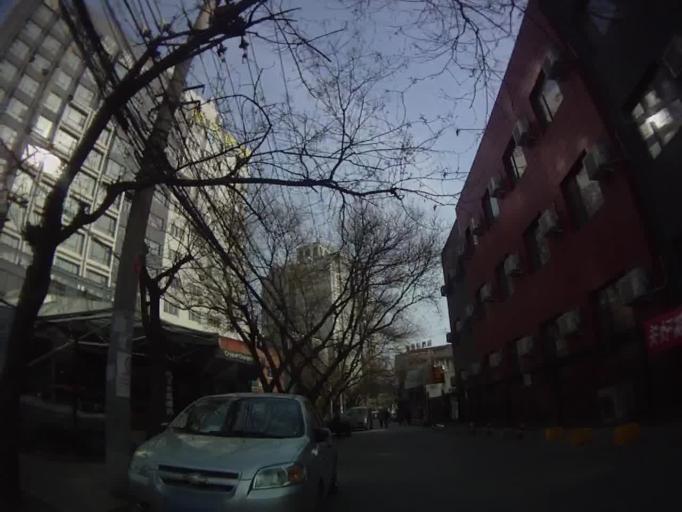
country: CN
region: Beijing
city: Chaowai
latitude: 39.9043
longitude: 116.4413
